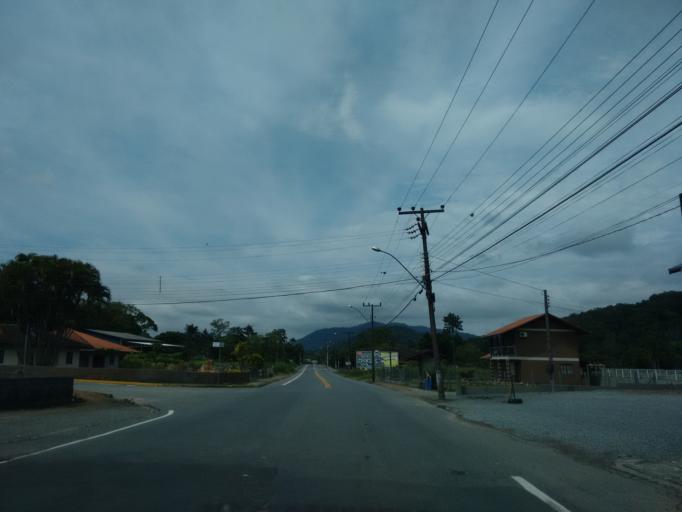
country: BR
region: Santa Catarina
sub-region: Pomerode
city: Pomerode
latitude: -26.6945
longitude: -49.1586
